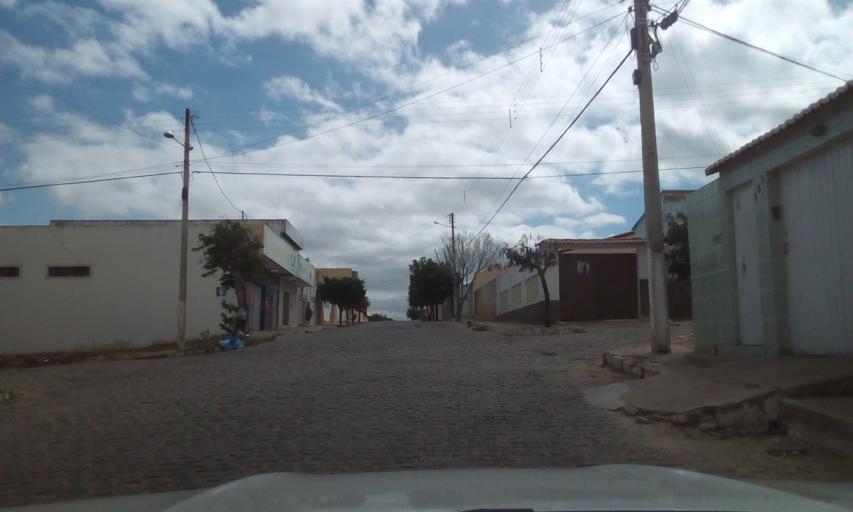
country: BR
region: Paraiba
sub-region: Picui
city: Picui
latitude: -6.5074
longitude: -36.3416
